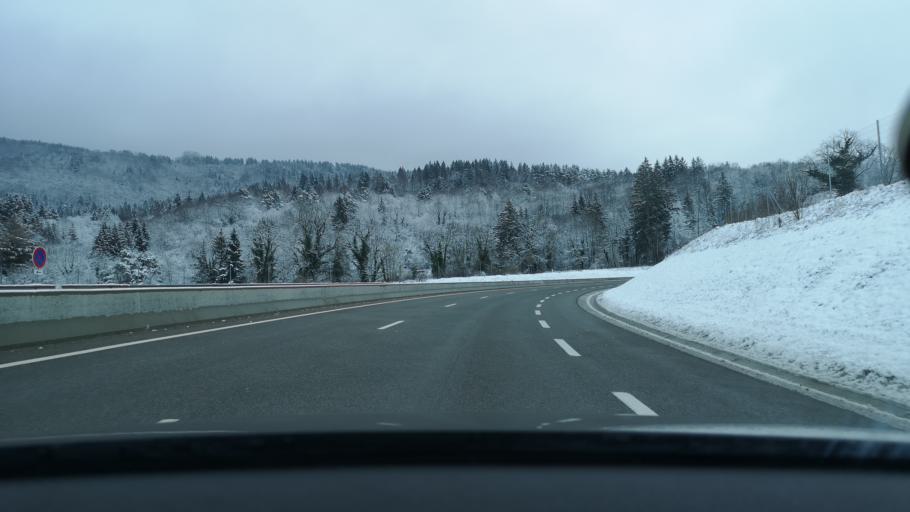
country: FR
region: Rhone-Alpes
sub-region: Departement de l'Ain
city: Dortan
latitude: 46.3231
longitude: 5.6733
